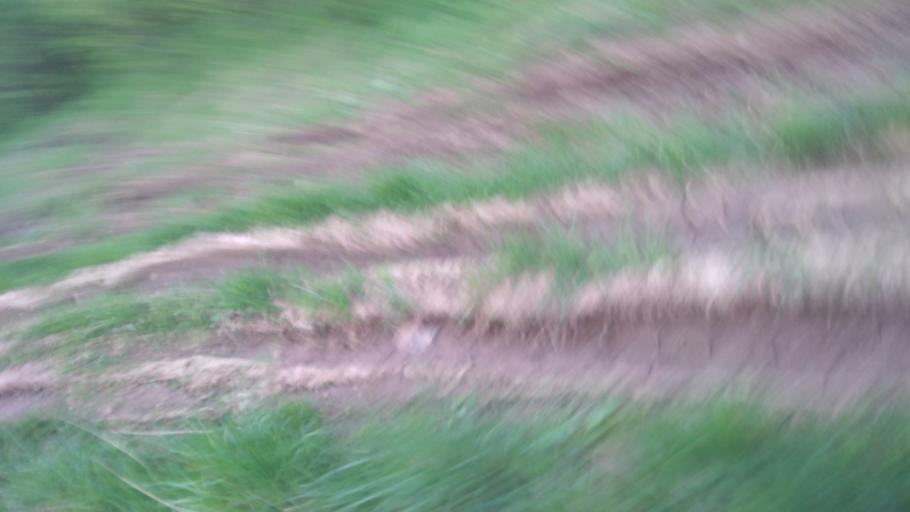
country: RU
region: Perm
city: Froly
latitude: 57.9676
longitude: 56.2916
